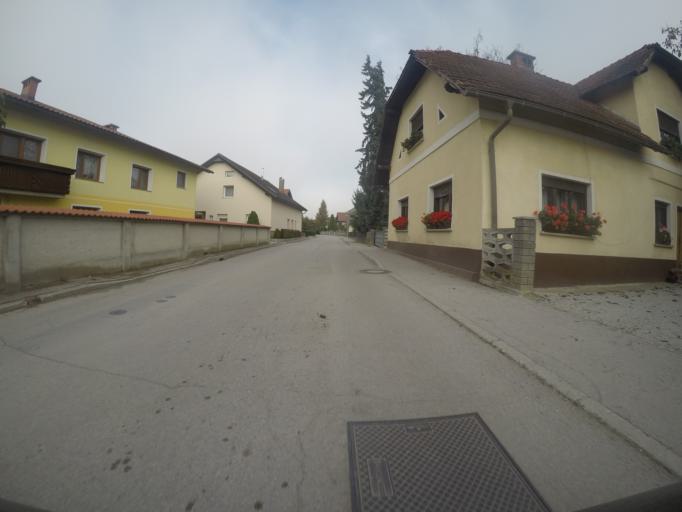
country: SI
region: Domzale
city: Dob
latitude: 46.1501
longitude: 14.6306
